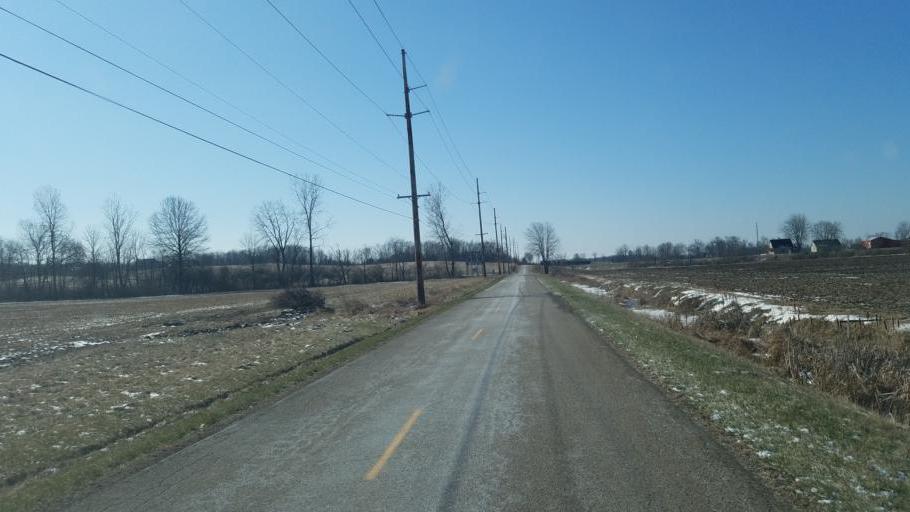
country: US
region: Ohio
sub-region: Knox County
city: Mount Vernon
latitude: 40.3276
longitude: -82.4718
